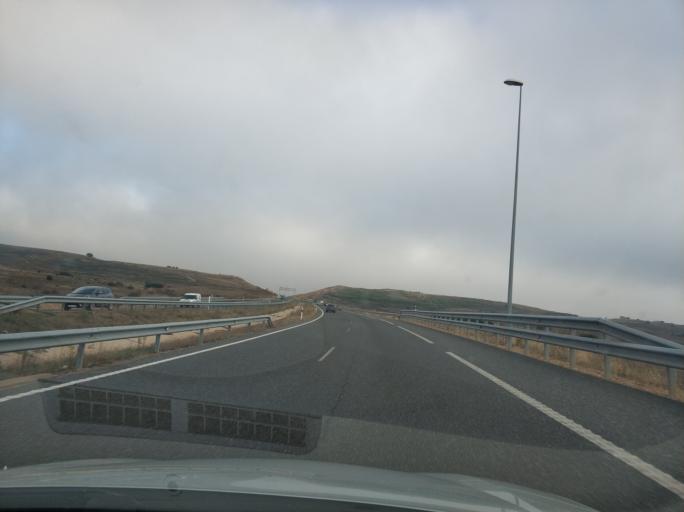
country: ES
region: Castille and Leon
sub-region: Provincia de Leon
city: Leon
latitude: 42.5645
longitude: -5.5402
